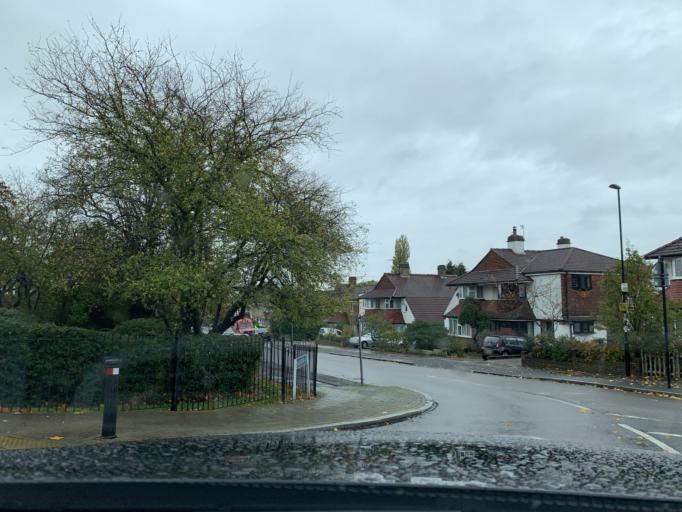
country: GB
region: England
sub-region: Greater London
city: Blackheath
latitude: 51.4373
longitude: 0.0224
